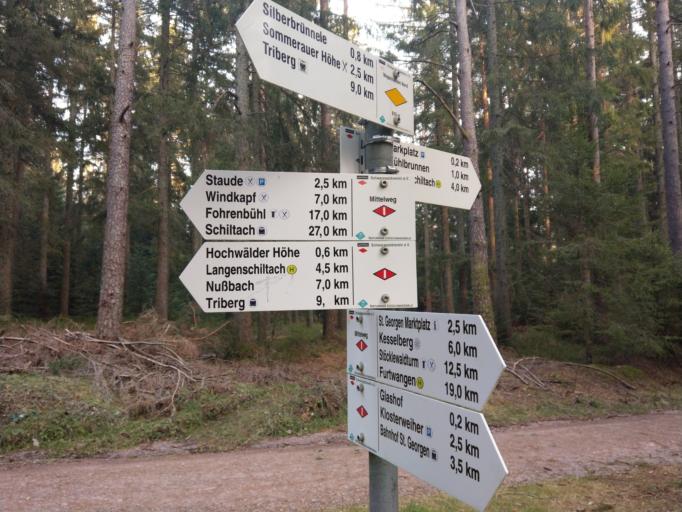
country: DE
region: Baden-Wuerttemberg
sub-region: Freiburg Region
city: Sankt Georgen im Schwarzwald
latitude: 48.1376
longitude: 8.3141
